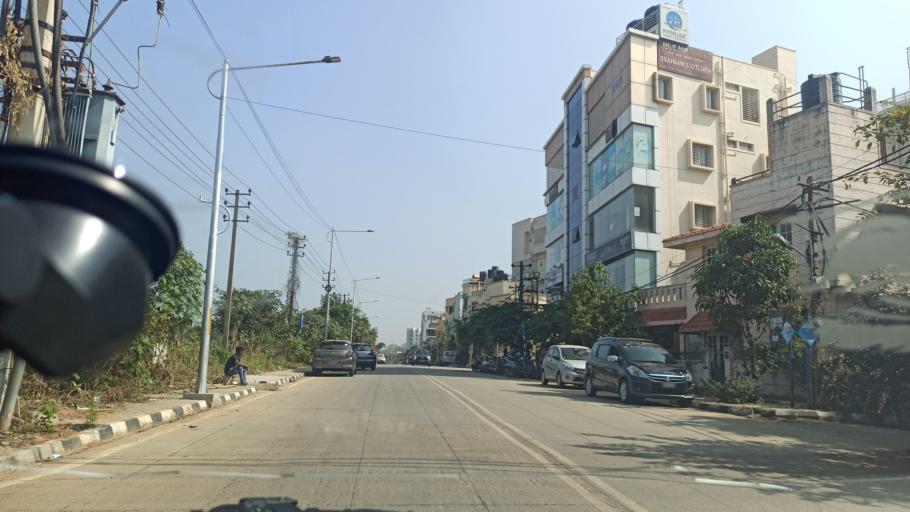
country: IN
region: Karnataka
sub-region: Bangalore Urban
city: Yelahanka
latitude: 13.0674
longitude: 77.5828
